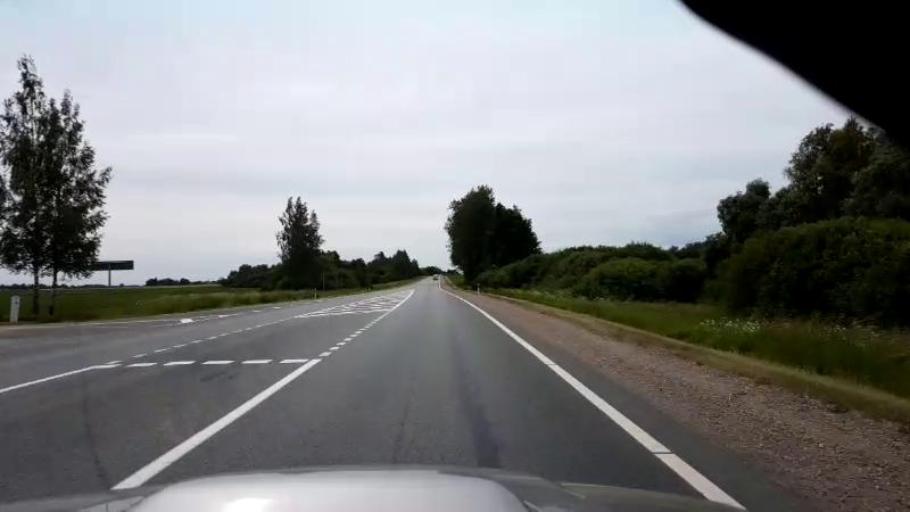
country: LV
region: Bauskas Rajons
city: Bauska
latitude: 56.4906
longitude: 24.1766
